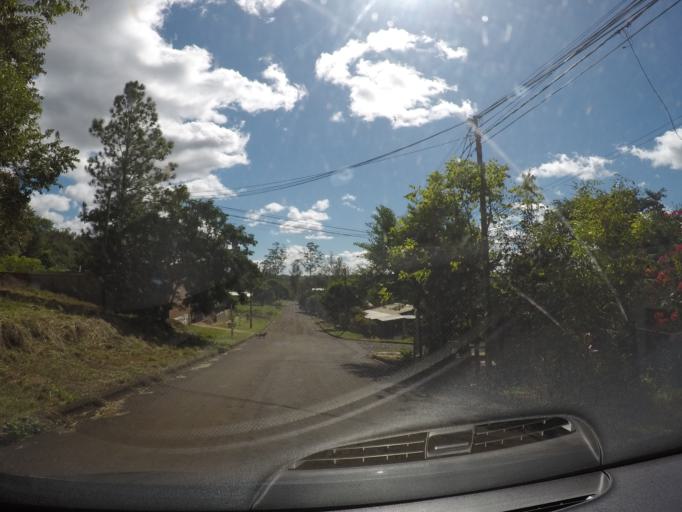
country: AR
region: Misiones
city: Puerto Rico
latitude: -26.7978
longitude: -55.0166
